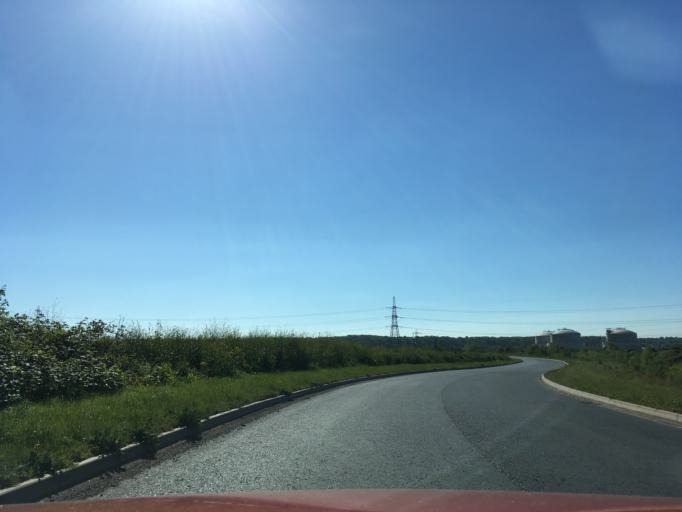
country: GB
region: England
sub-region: South Gloucestershire
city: Severn Beach
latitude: 51.5405
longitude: -2.6635
